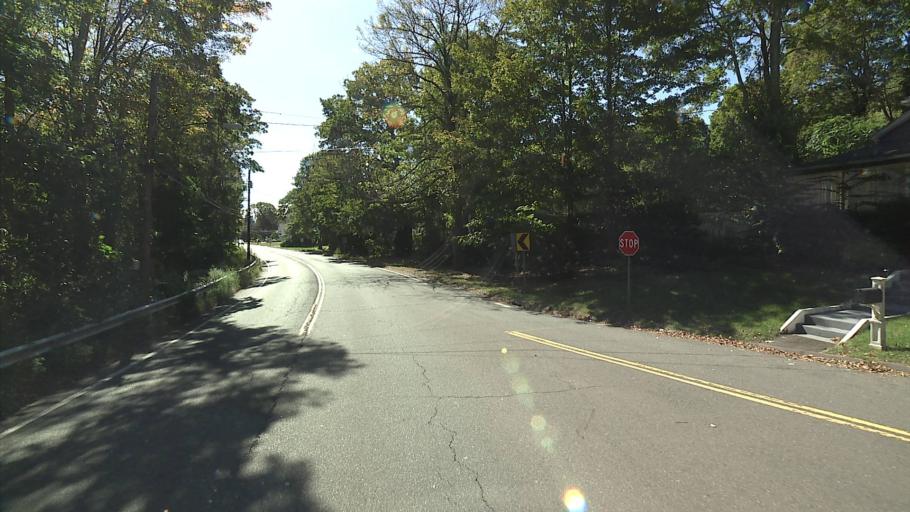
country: US
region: Connecticut
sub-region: New Haven County
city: Woodbridge
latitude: 41.3518
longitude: -72.9845
